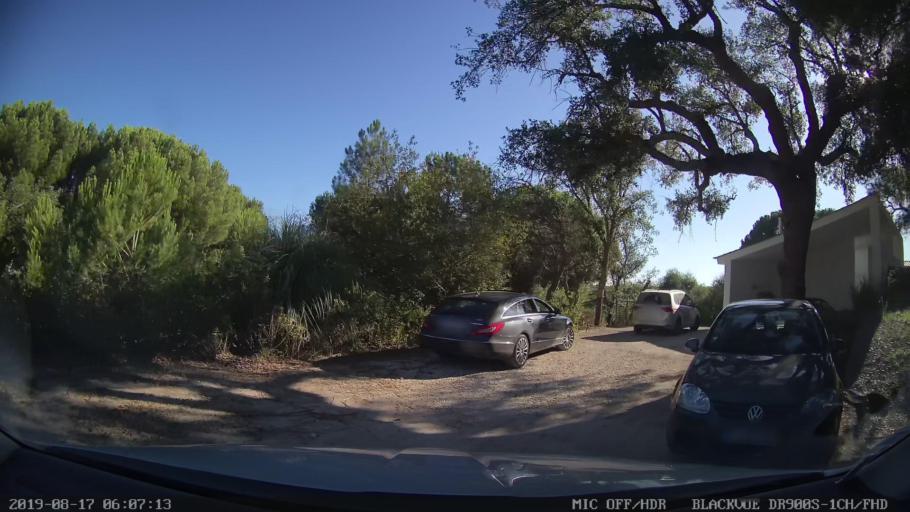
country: PT
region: Santarem
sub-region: Benavente
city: Poceirao
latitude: 38.8452
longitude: -8.6954
